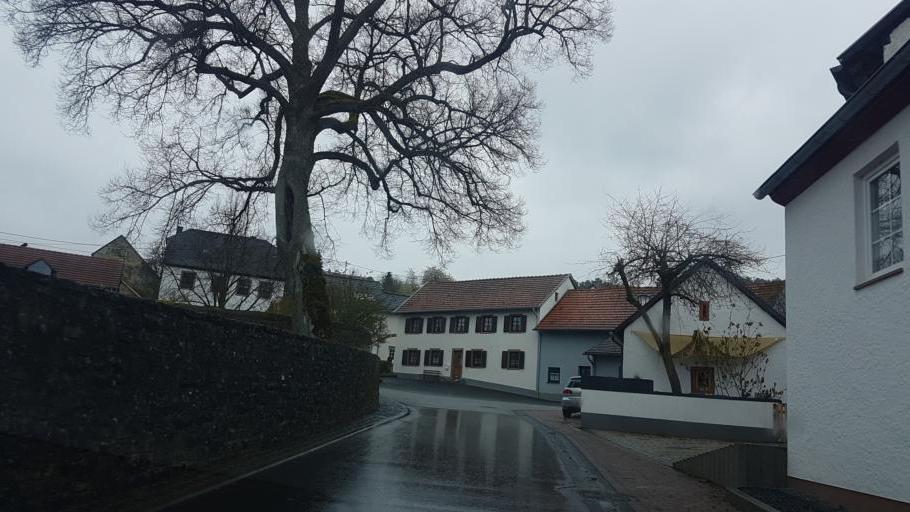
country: DE
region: Rheinland-Pfalz
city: Oberehe-Stroheich
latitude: 50.3121
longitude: 6.7541
